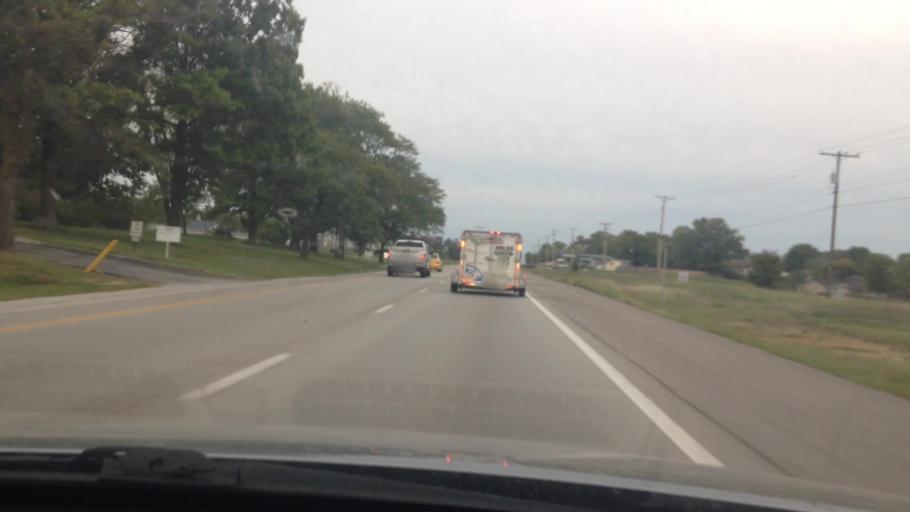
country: US
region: Missouri
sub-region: Jackson County
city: Raytown
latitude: 38.9817
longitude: -94.4585
